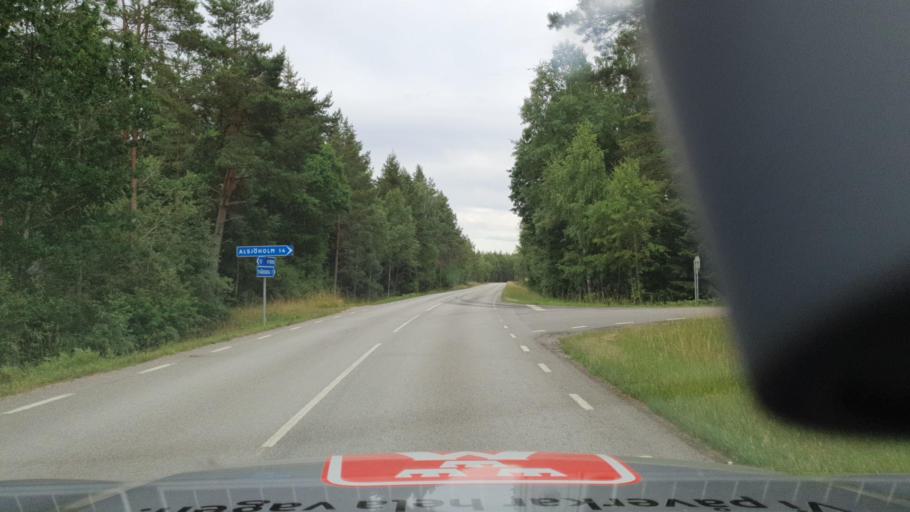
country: SE
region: Kalmar
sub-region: Nybro Kommun
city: Nybro
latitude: 56.6718
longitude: 15.9902
